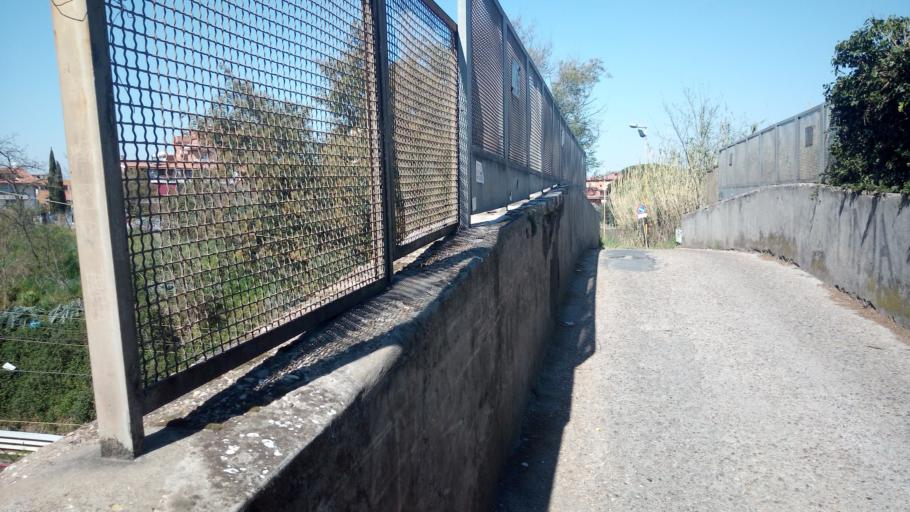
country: IT
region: Latium
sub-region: Citta metropolitana di Roma Capitale
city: Ciampino
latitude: 41.8029
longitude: 12.6049
